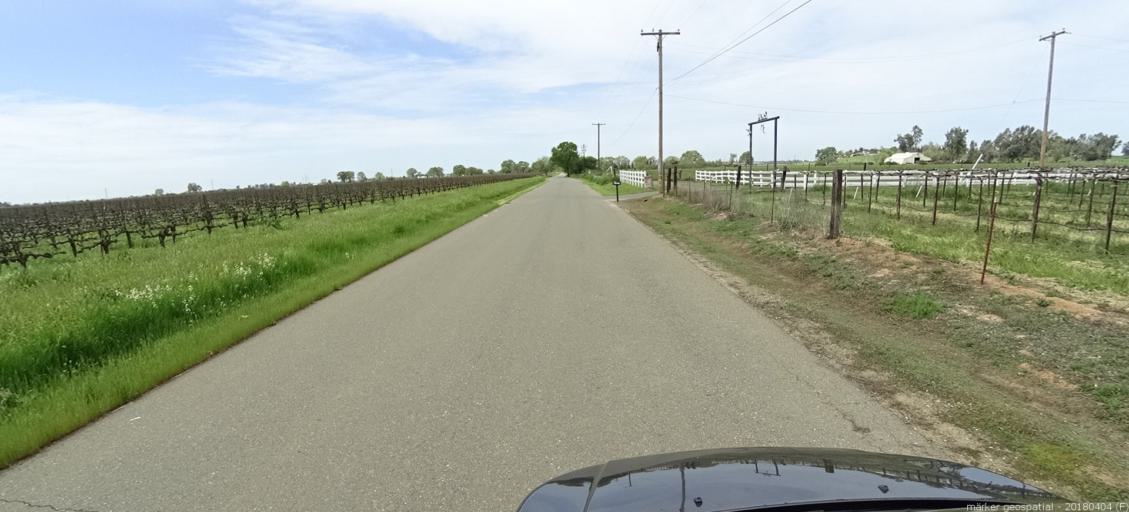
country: US
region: California
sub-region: Sacramento County
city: Clay
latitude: 38.2780
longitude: -121.1823
